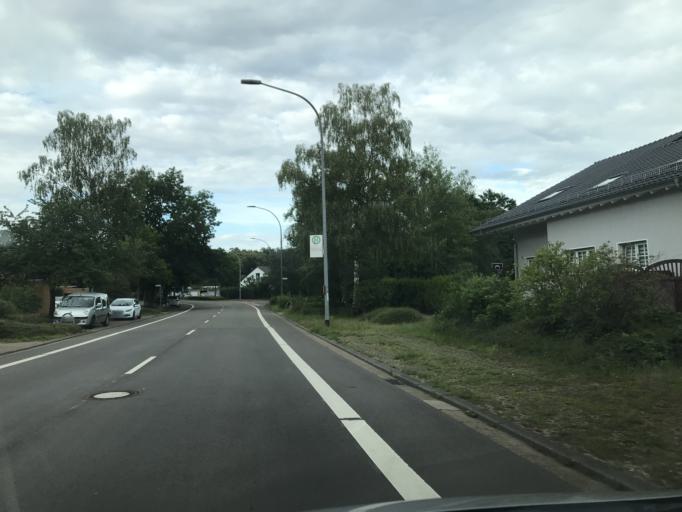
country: DE
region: Saarland
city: Saarwellingen
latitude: 49.3364
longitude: 6.7821
